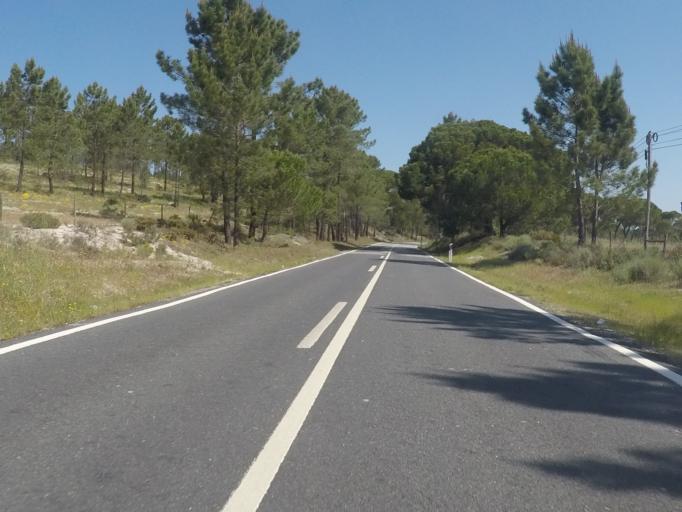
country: PT
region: Setubal
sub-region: Grandola
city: Grandola
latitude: 38.2943
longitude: -8.7267
